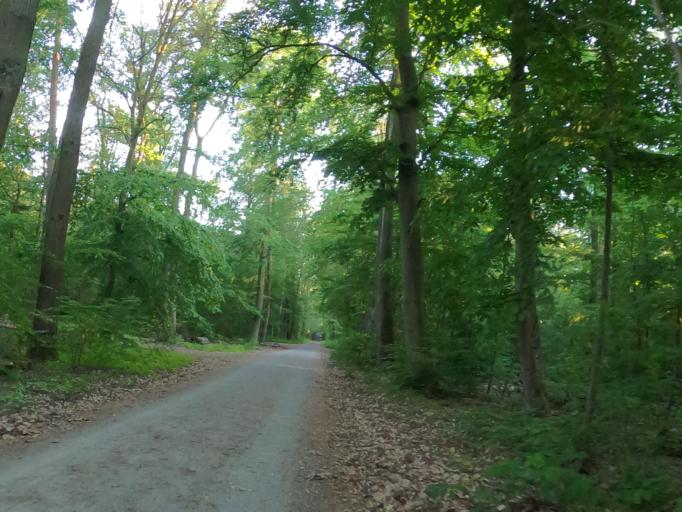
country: DE
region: Hesse
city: Kelsterbach
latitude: 50.0574
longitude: 8.5546
